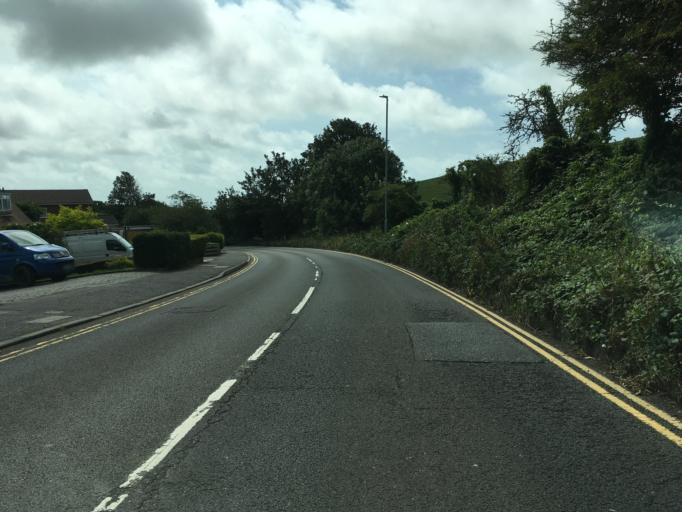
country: GB
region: England
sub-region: Brighton and Hove
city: Rottingdean
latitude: 50.8333
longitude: -0.0751
